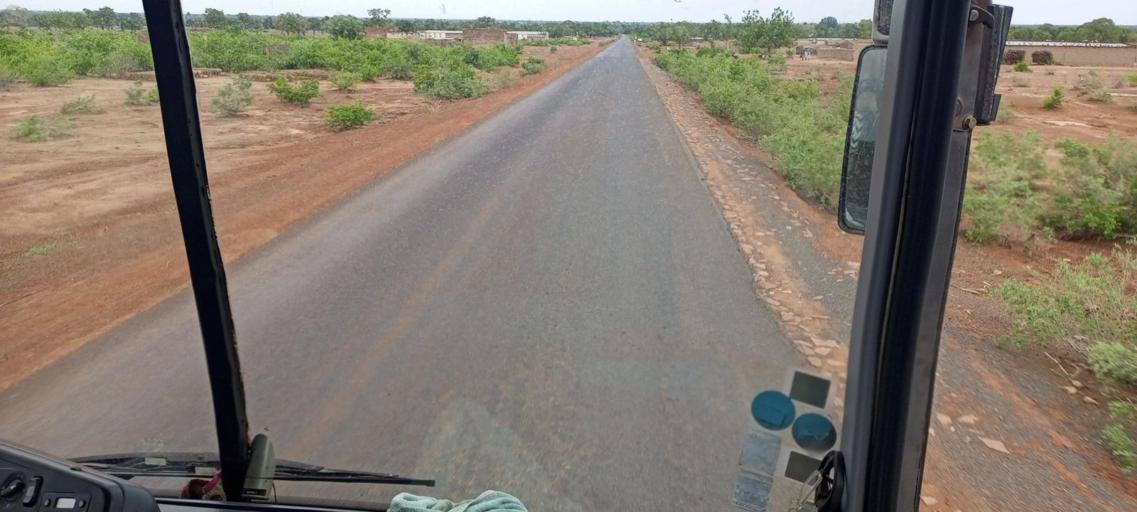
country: ML
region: Segou
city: Bla
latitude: 12.6905
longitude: -5.7237
